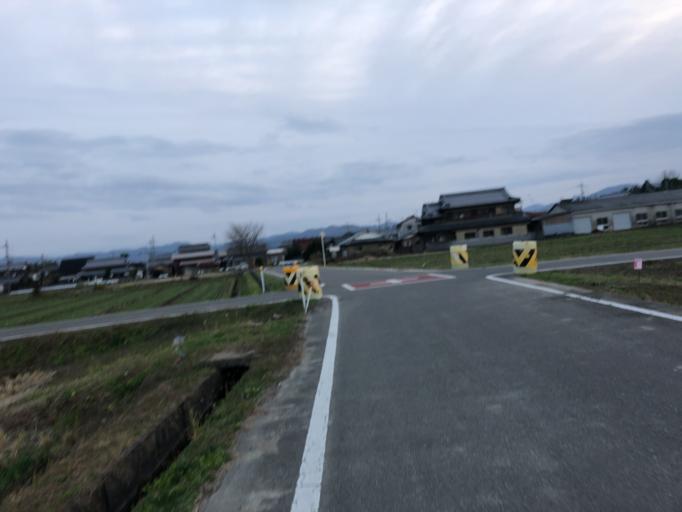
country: JP
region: Kyoto
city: Kameoka
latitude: 35.0595
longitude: 135.5618
